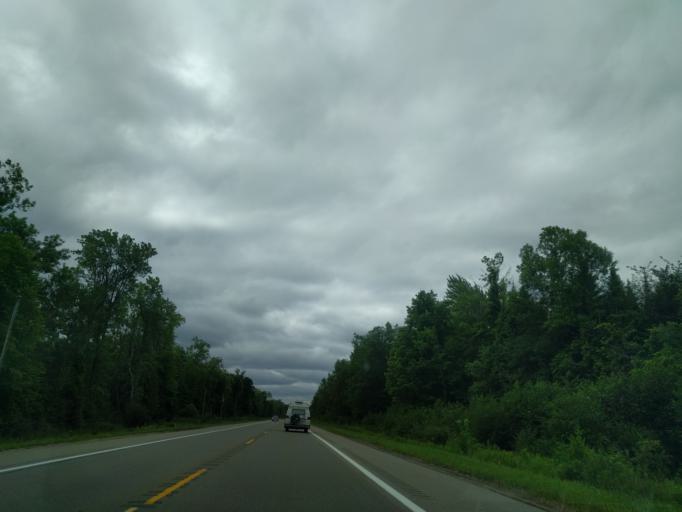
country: US
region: Michigan
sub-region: Menominee County
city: Menominee
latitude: 45.2257
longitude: -87.5129
